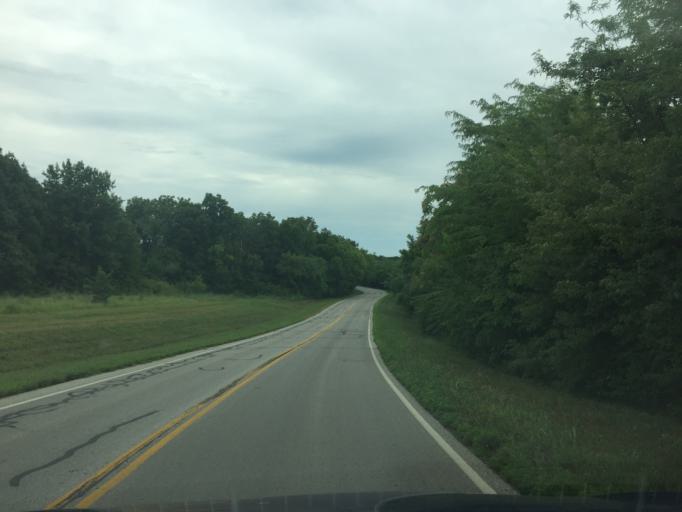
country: US
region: Missouri
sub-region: Platte County
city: Weston
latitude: 39.3691
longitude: -94.9389
